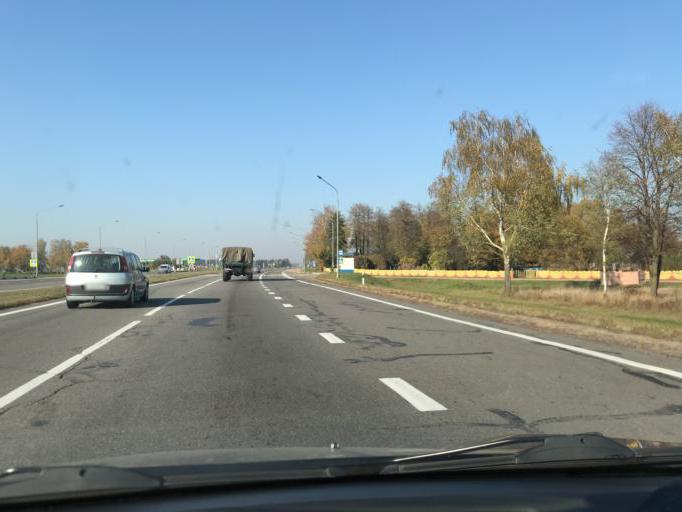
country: BY
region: Minsk
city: Dukora
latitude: 53.7031
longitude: 27.8810
